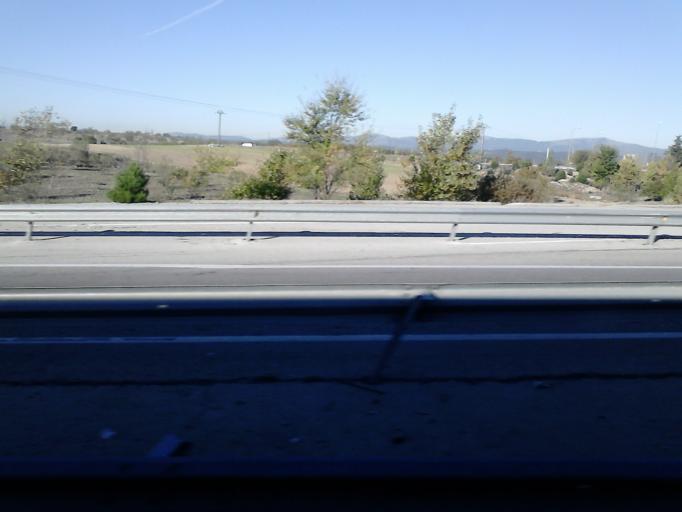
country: ES
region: Madrid
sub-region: Provincia de Madrid
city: Las Rozas de Madrid
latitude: 40.4988
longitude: -3.8970
